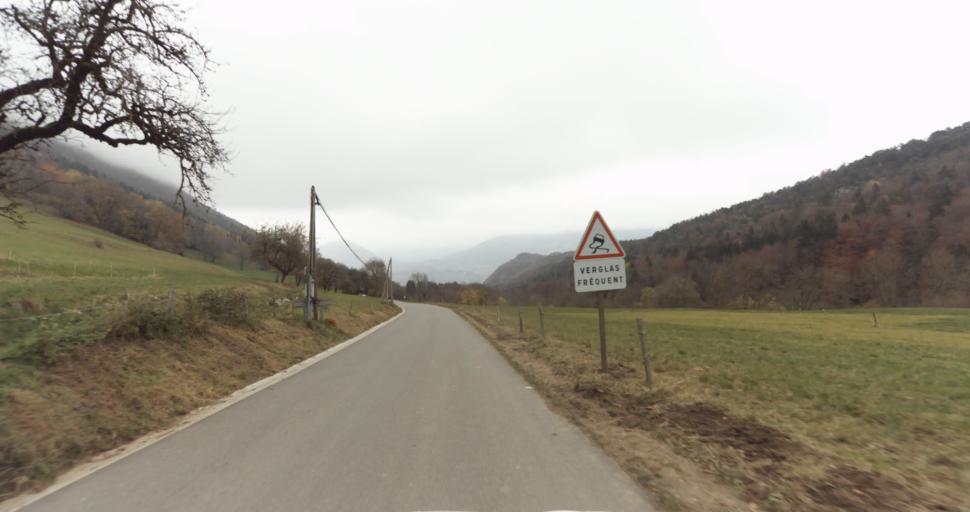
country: FR
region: Rhone-Alpes
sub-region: Departement de la Haute-Savoie
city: Doussard
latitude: 45.8010
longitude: 6.1901
